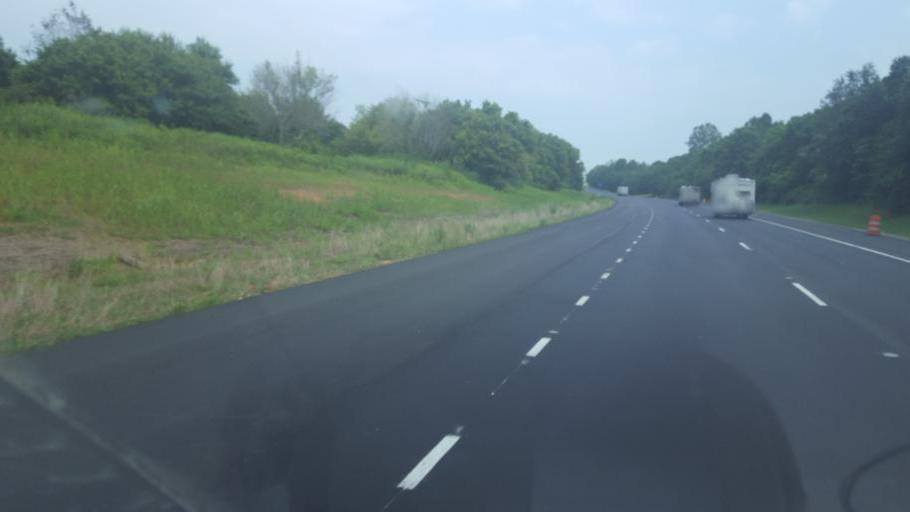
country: US
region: North Carolina
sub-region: Iredell County
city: Statesville
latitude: 35.9054
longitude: -80.8541
